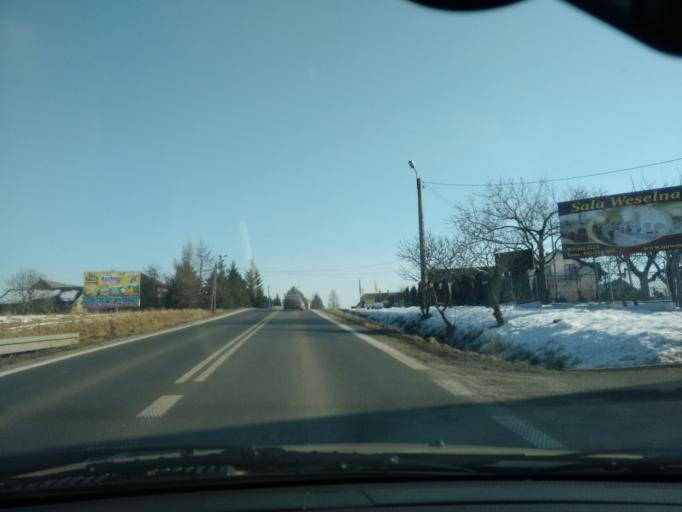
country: PL
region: Lesser Poland Voivodeship
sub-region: Powiat oswiecimski
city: Bulowice
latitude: 49.8735
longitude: 19.2968
